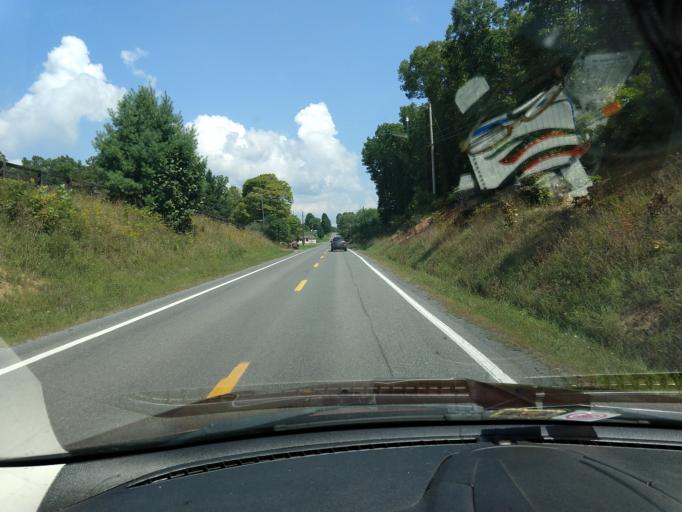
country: US
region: West Virginia
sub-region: Greenbrier County
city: Fairlea
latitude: 37.8435
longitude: -80.5531
